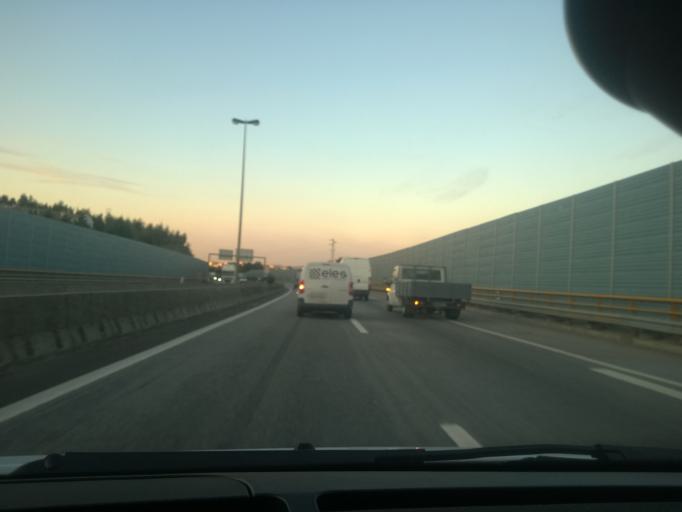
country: PT
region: Porto
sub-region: Vila Nova de Gaia
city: Avintes
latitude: 41.1055
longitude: -8.5659
